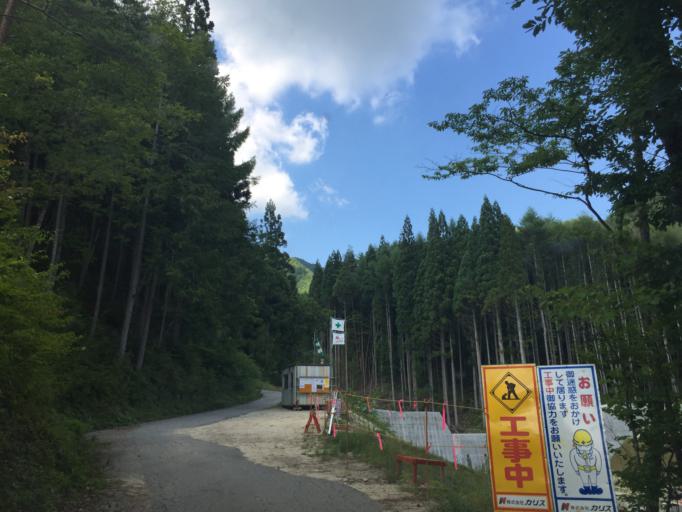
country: JP
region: Nagano
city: Iida
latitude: 35.3774
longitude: 137.6949
